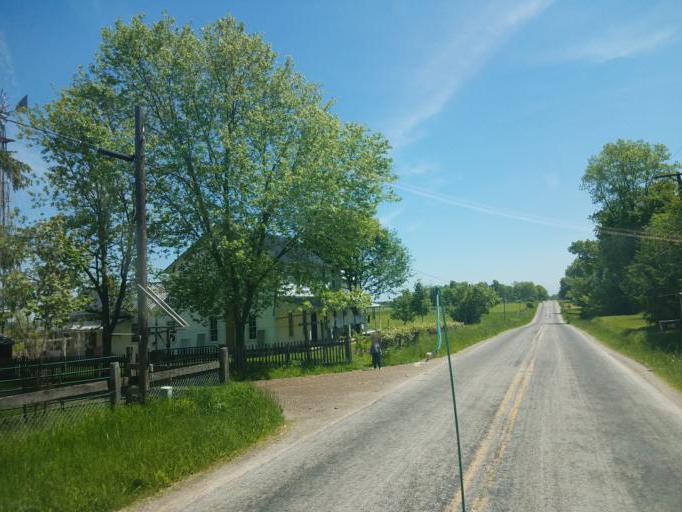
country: US
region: Ohio
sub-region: Wayne County
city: West Salem
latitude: 40.9447
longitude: -82.1824
